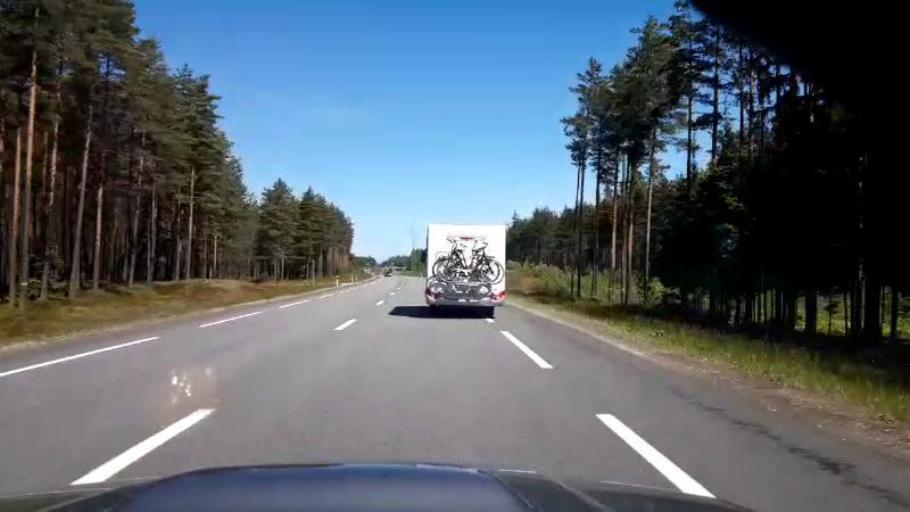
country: LV
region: Saulkrastu
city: Saulkrasti
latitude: 57.2395
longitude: 24.4272
